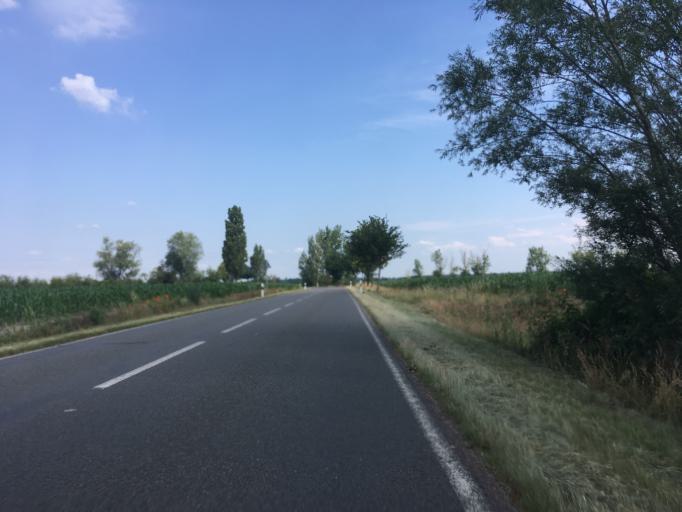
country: DE
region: Saxony-Anhalt
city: Quellendorf
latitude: 51.7752
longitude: 12.0979
